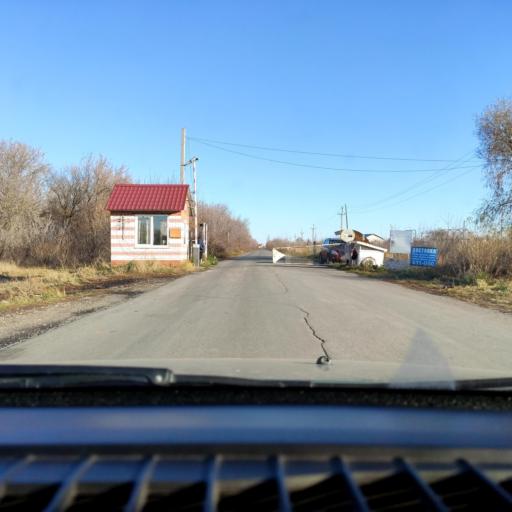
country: RU
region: Samara
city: Tol'yatti
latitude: 53.6593
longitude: 49.3328
